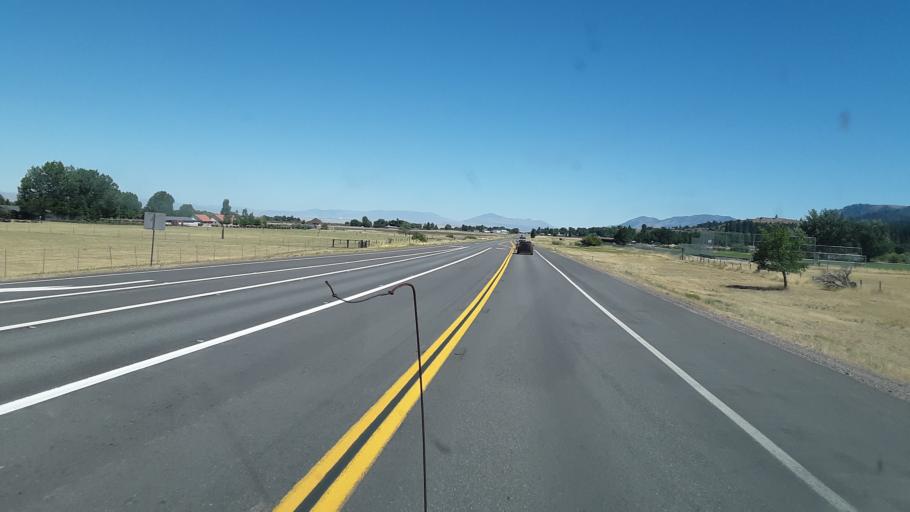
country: US
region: California
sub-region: Lassen County
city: Janesville
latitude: 40.3028
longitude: -120.5239
